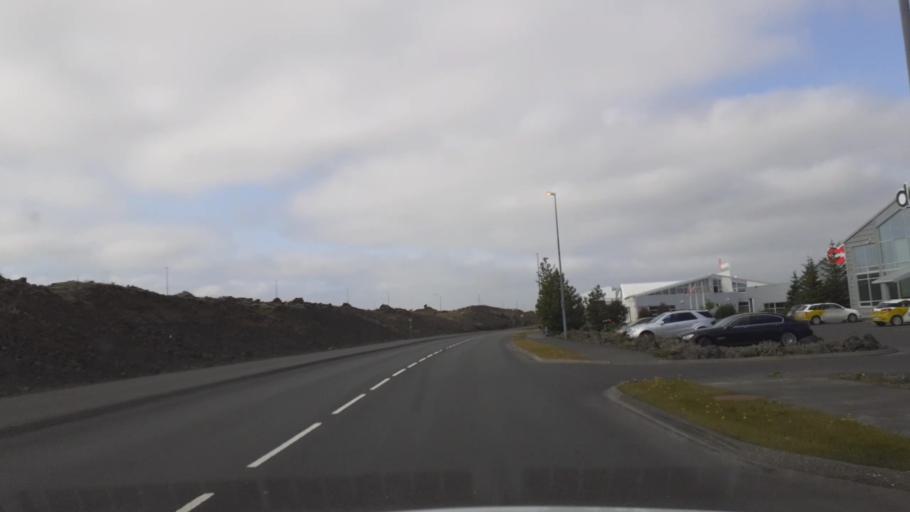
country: IS
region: Capital Region
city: Gardabaer
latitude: 64.0765
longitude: -21.9212
